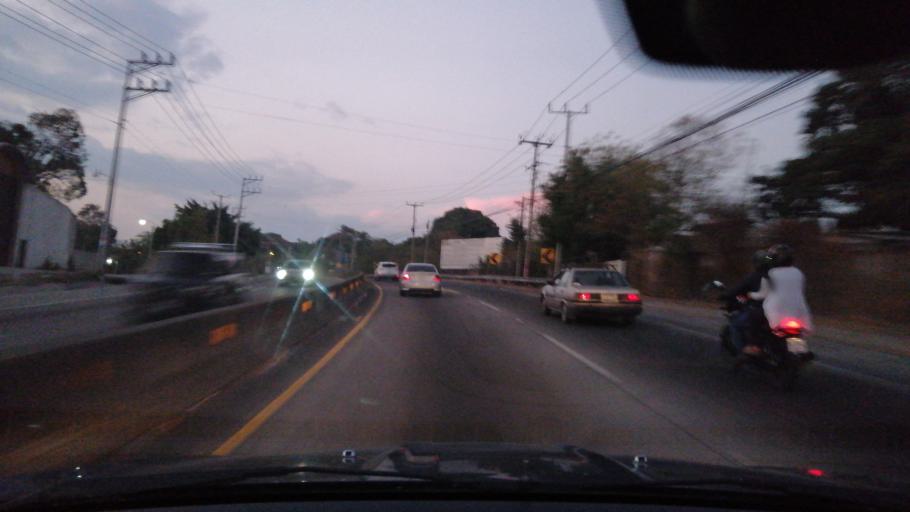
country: SV
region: San Salvador
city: Mejicanos
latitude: 13.7427
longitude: -89.2172
